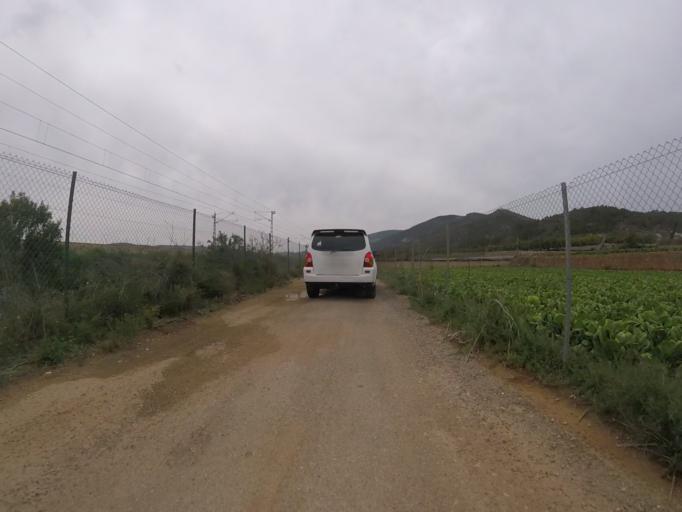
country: ES
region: Valencia
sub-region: Provincia de Castello
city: Alcoceber
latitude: 40.2543
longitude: 0.2520
